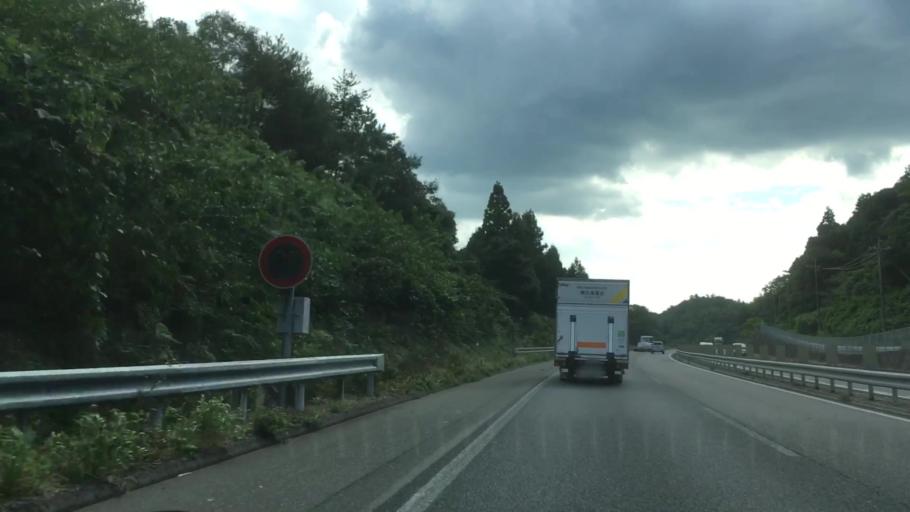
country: JP
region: Yamaguchi
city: Iwakuni
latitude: 34.1367
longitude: 132.1170
